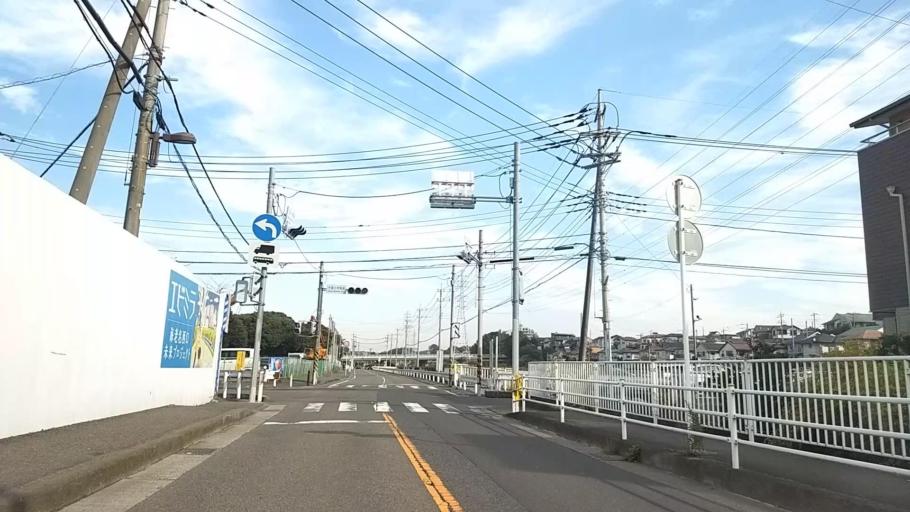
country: JP
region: Kanagawa
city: Zama
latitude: 35.4599
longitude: 139.3924
